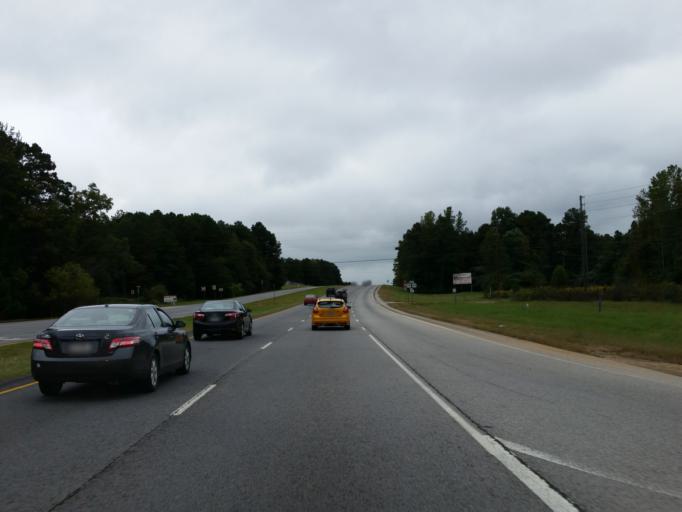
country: US
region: Georgia
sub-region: Henry County
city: Hampton
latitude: 33.3699
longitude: -84.2965
